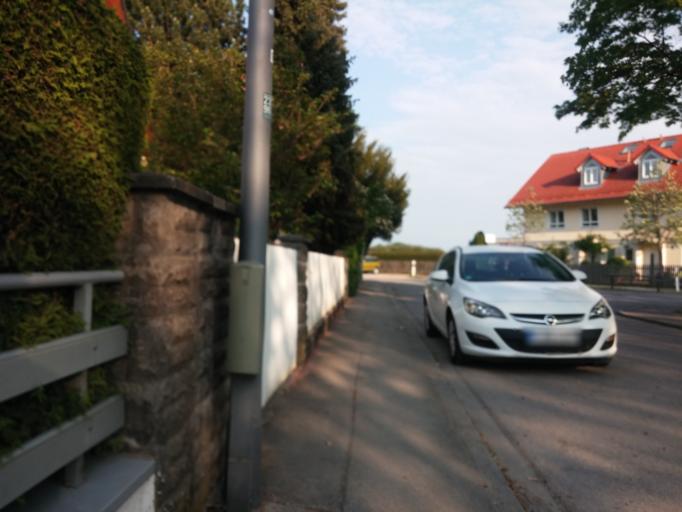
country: DE
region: Bavaria
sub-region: Upper Bavaria
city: Haar
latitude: 48.1264
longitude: 11.6775
